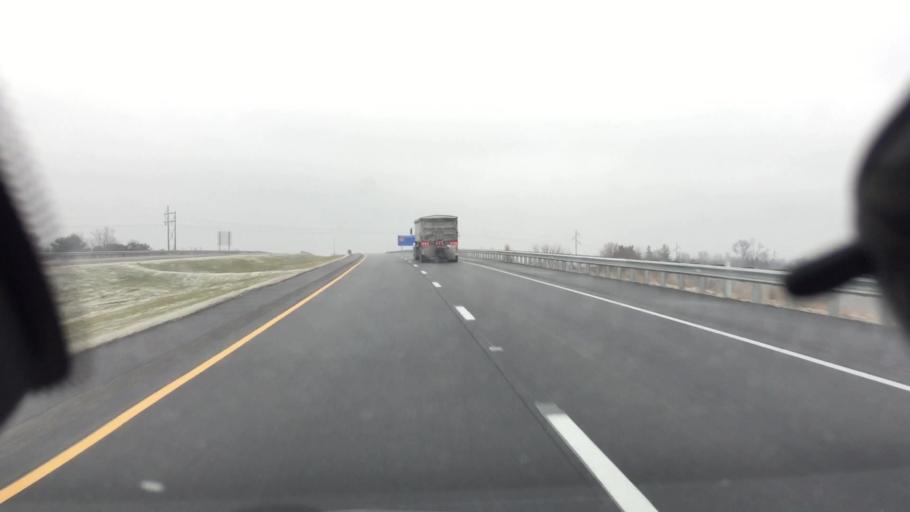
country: US
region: Illinois
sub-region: Knox County
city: Galesburg
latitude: 40.9760
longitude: -90.3356
